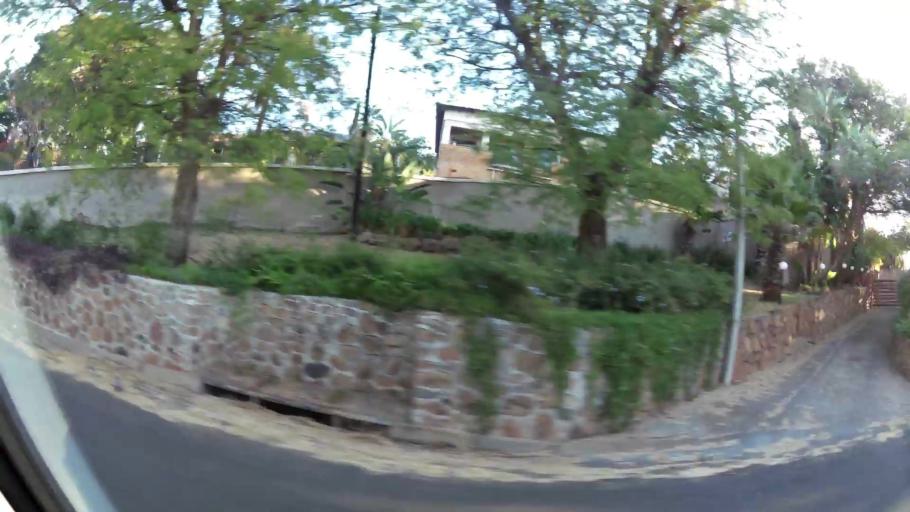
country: ZA
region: North-West
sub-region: Bojanala Platinum District Municipality
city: Rustenburg
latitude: -25.6918
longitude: 27.2116
